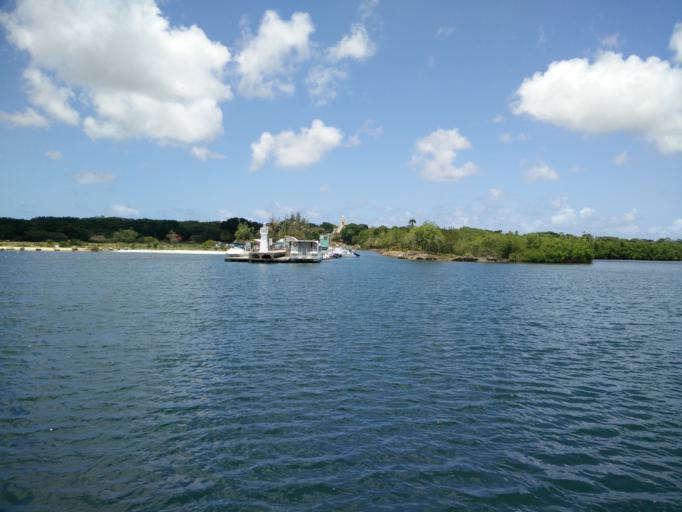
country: GP
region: Guadeloupe
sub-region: Guadeloupe
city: Petit-Canal
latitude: 16.3777
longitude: -61.4977
